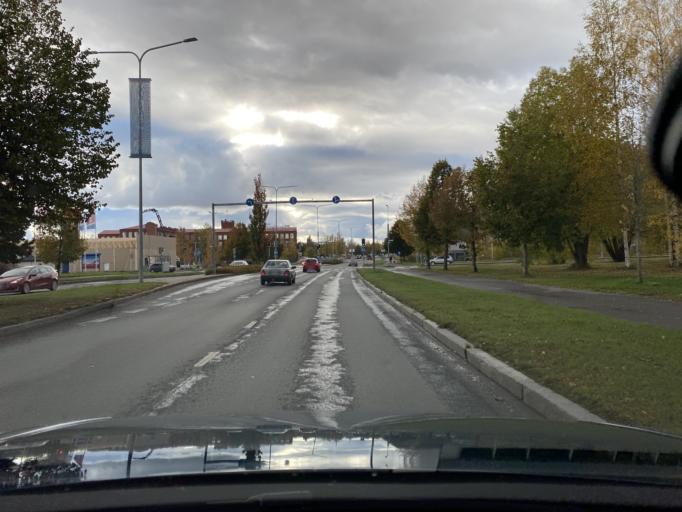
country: FI
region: Haeme
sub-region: Forssa
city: Forssa
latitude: 60.8126
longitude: 23.6327
